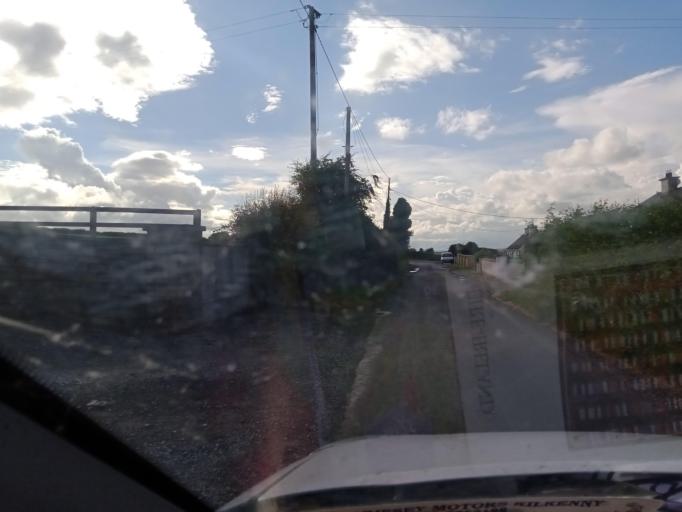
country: IE
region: Leinster
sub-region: Laois
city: Rathdowney
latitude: 52.7718
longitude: -7.4996
